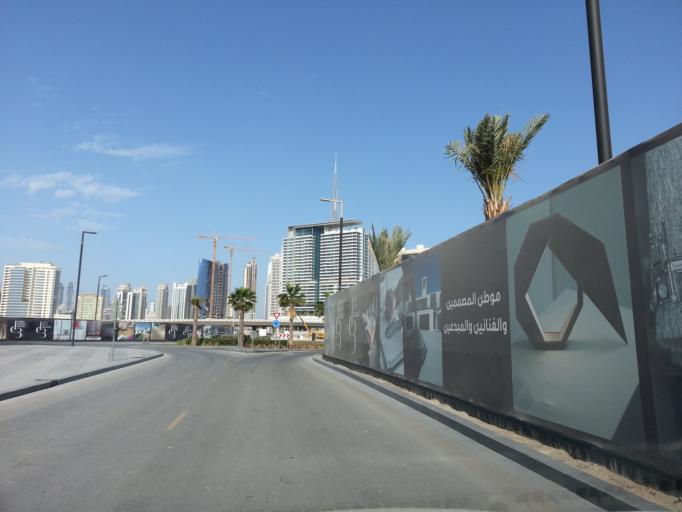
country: AE
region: Dubai
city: Dubai
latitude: 25.1904
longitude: 55.2971
